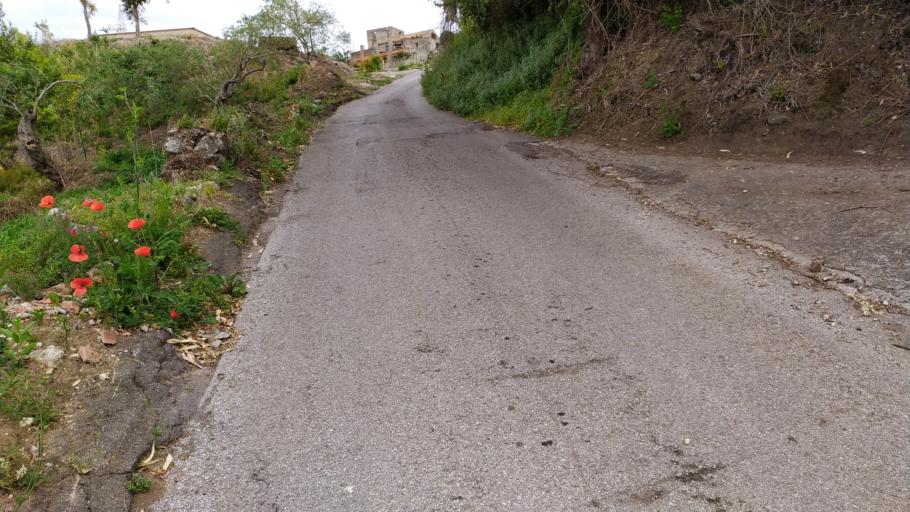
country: IT
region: Sicily
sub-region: Messina
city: San Filippo del Mela
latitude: 38.1693
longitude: 15.2845
